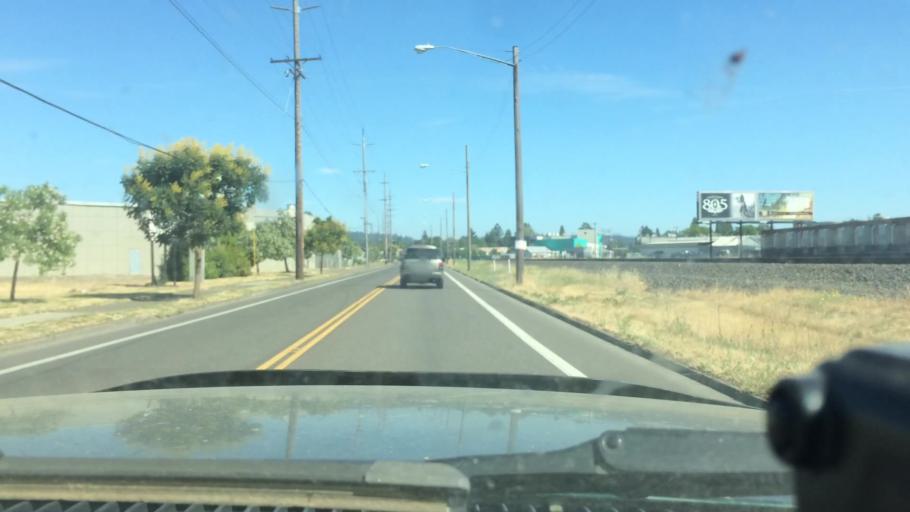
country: US
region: Oregon
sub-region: Lane County
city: Eugene
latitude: 44.0613
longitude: -123.1150
